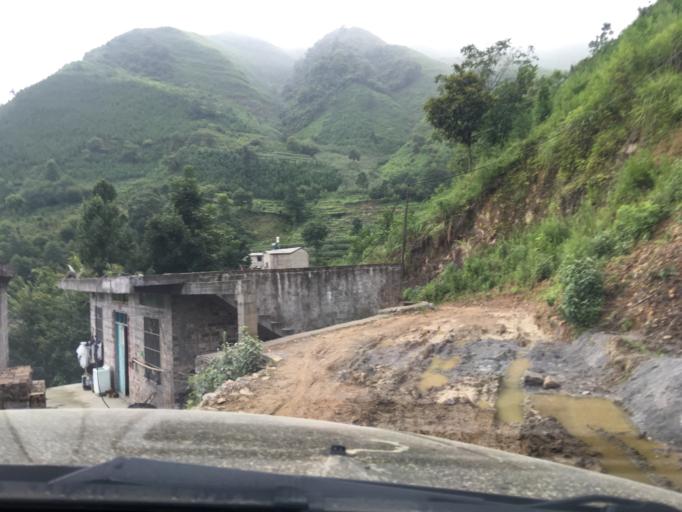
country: CN
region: Guangxi Zhuangzu Zizhiqu
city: Xinzhou
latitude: 24.9891
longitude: 105.6387
